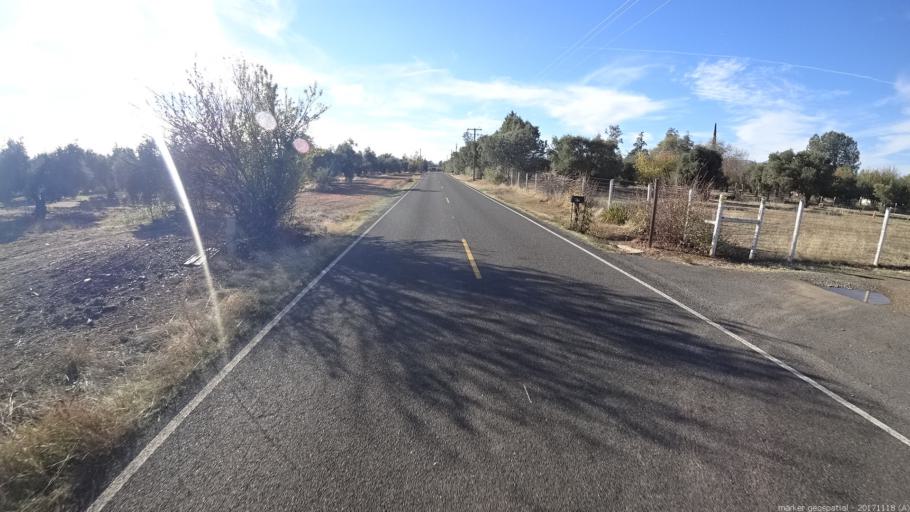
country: US
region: California
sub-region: Shasta County
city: Anderson
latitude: 40.4460
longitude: -122.4316
